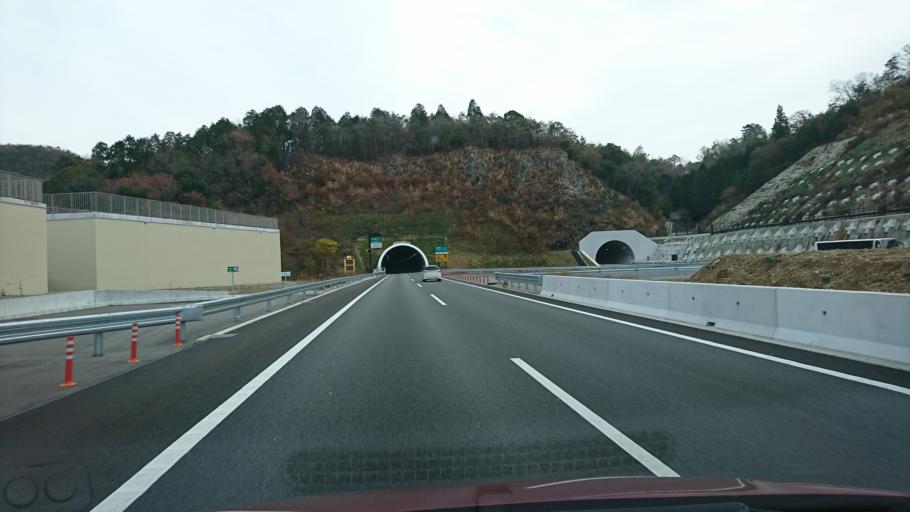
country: JP
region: Hyogo
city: Takarazuka
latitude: 34.8732
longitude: 135.3221
